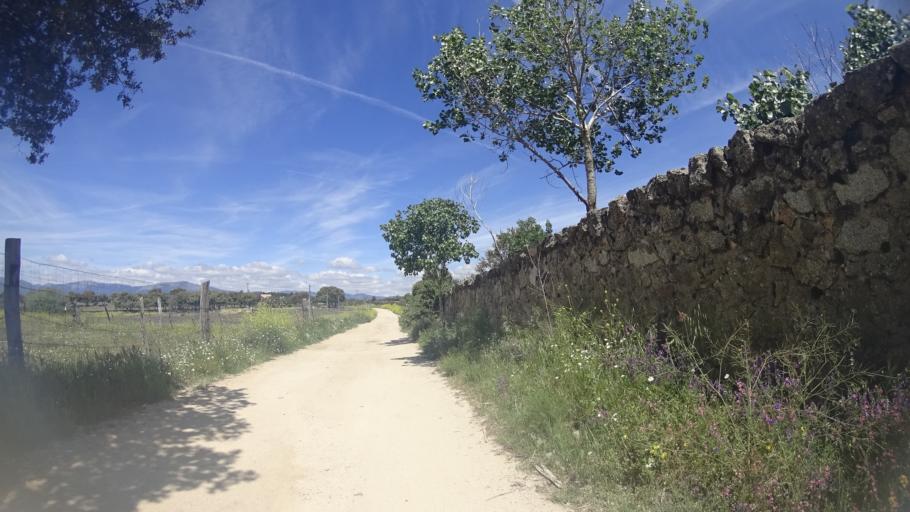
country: ES
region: Madrid
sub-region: Provincia de Madrid
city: Galapagar
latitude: 40.5625
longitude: -3.9932
